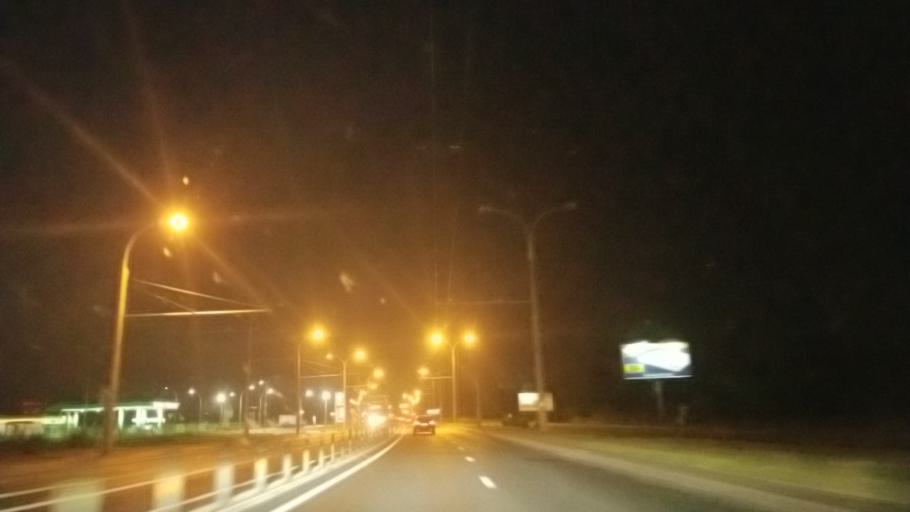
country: BY
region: Brest
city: Brest
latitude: 52.0789
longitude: 23.7698
